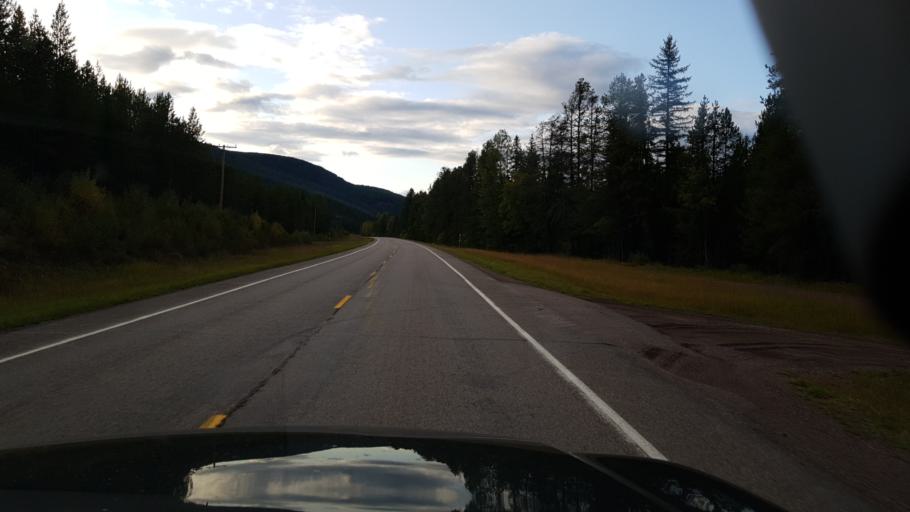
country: US
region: Montana
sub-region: Flathead County
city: Columbia Falls
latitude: 48.3838
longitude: -113.6930
